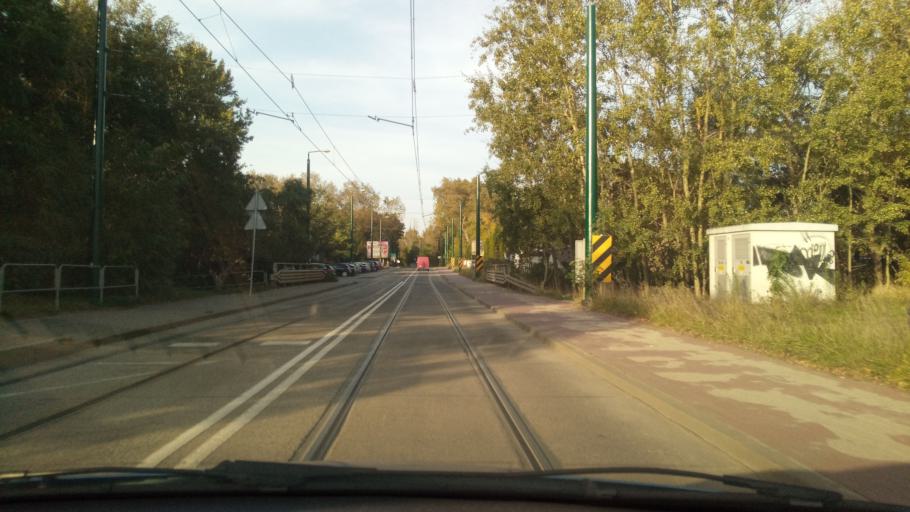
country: PL
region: Silesian Voivodeship
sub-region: Sosnowiec
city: Sosnowiec
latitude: 50.2696
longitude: 19.1113
